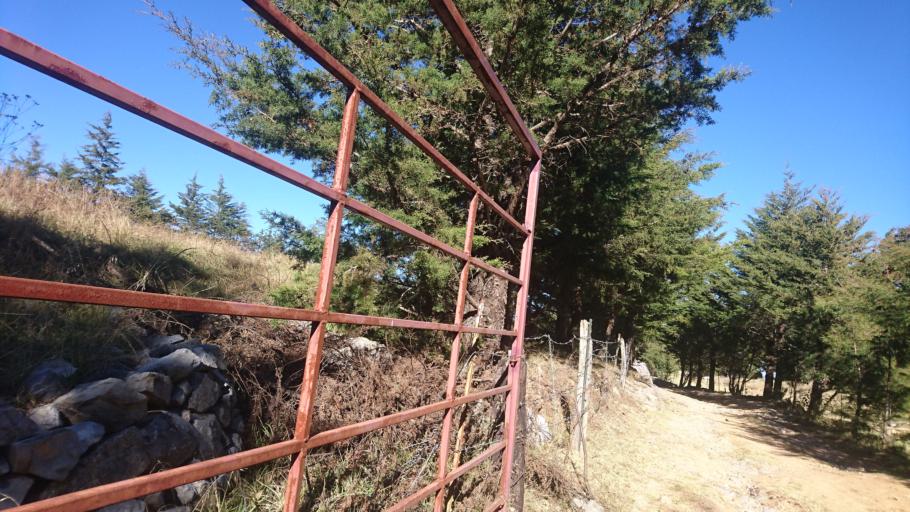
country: MX
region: San Luis Potosi
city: Zaragoza
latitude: 22.0193
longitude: -100.6048
